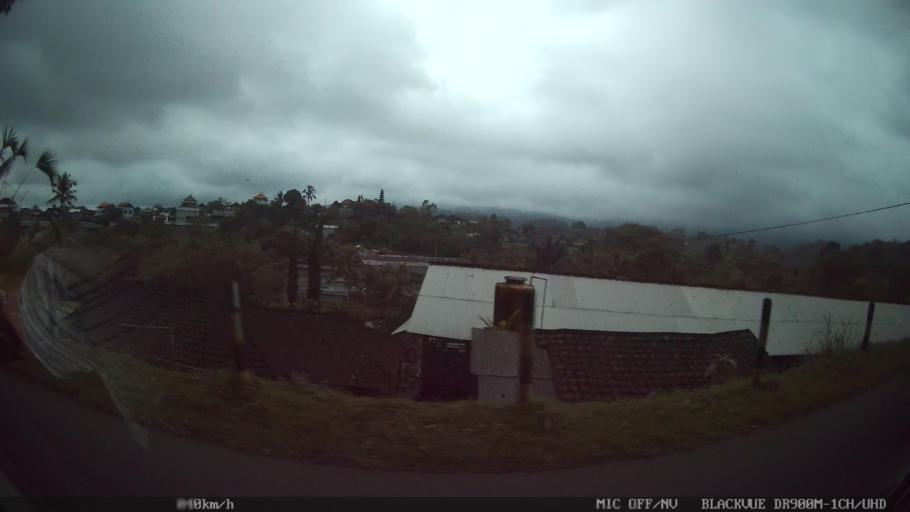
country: ID
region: Bali
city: Empalan
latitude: -8.3817
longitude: 115.1495
